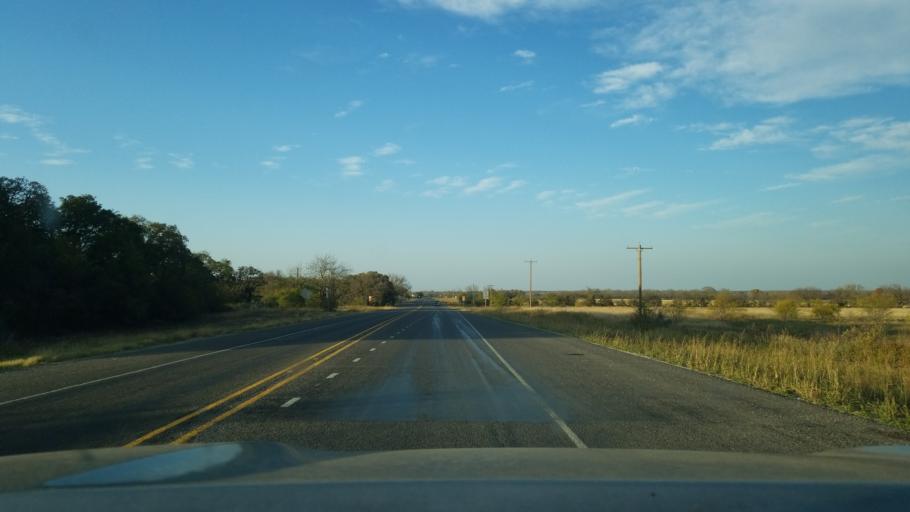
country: US
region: Texas
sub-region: Eastland County
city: Cisco
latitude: 32.1109
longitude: -98.9643
